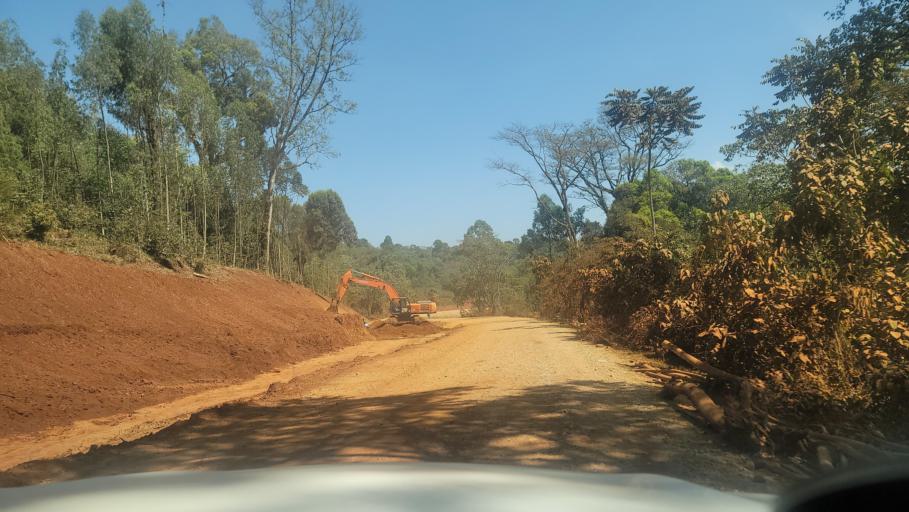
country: ET
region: Oromiya
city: Agaro
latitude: 7.7877
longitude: 36.4019
